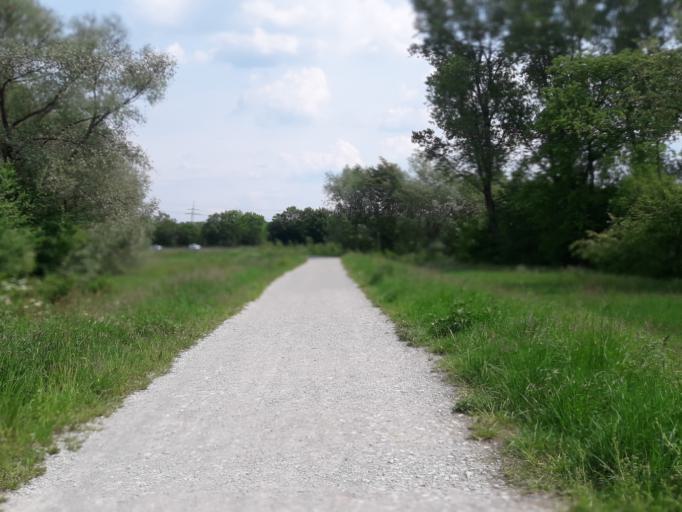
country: DE
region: North Rhine-Westphalia
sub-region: Regierungsbezirk Detmold
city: Paderborn
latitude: 51.7568
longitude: 8.7566
